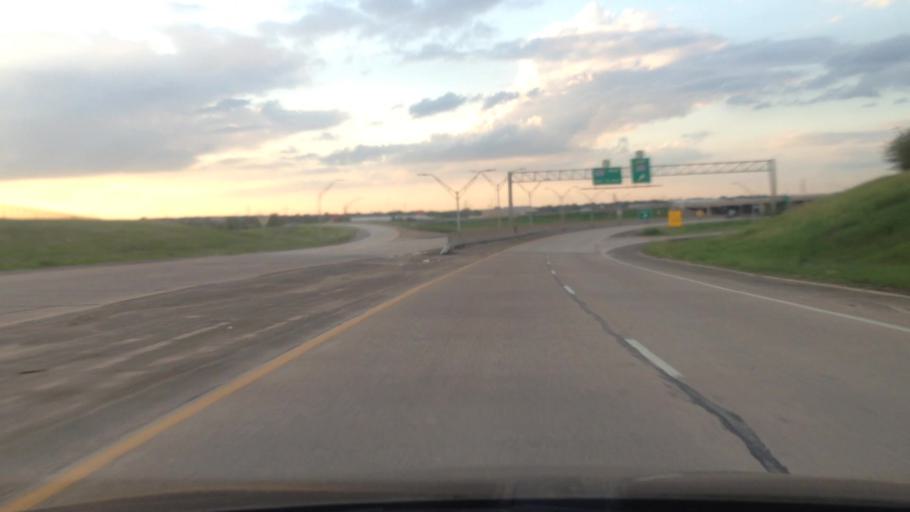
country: US
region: Texas
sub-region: Tarrant County
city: Saginaw
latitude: 32.8324
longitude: -97.3609
